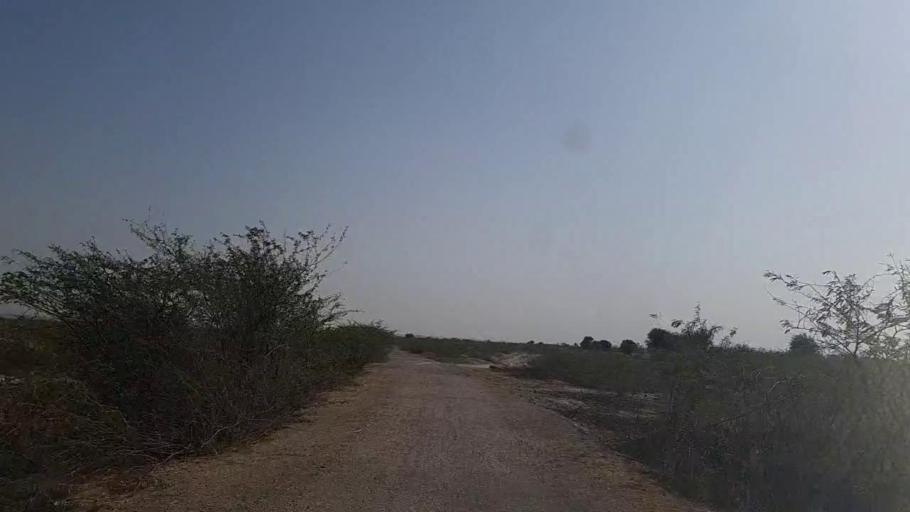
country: PK
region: Sindh
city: Kadhan
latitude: 24.5934
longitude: 69.2628
